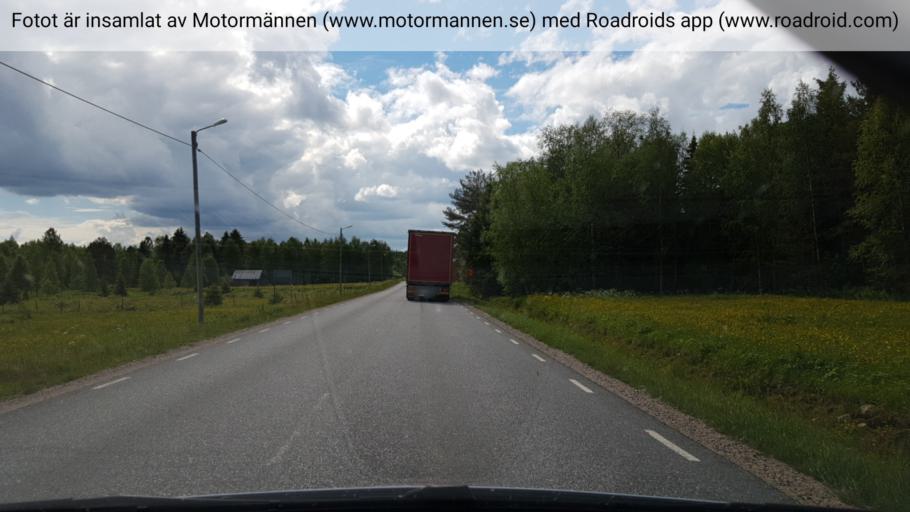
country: FI
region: Lapland
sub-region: Torniolaakso
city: Ylitornio
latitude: 66.2691
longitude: 23.6521
